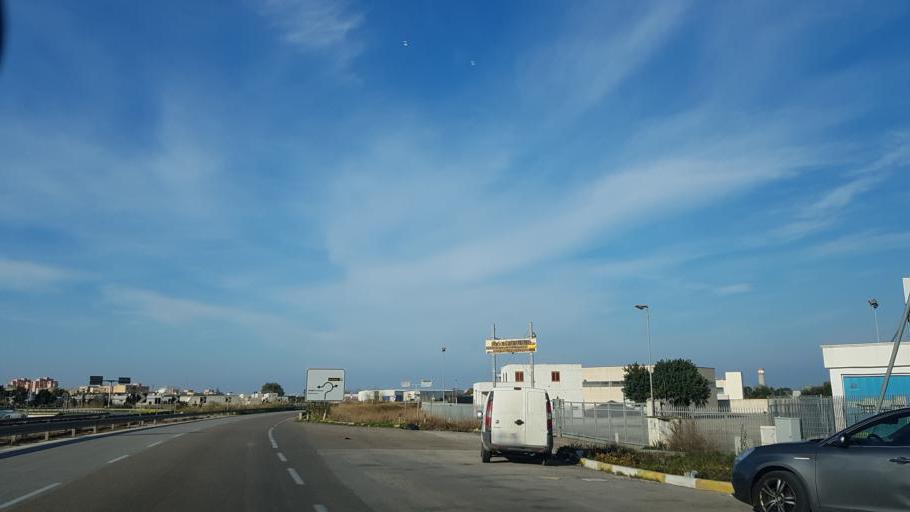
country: IT
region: Apulia
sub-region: Provincia di Brindisi
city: La Rosa
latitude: 40.6231
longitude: 17.9573
